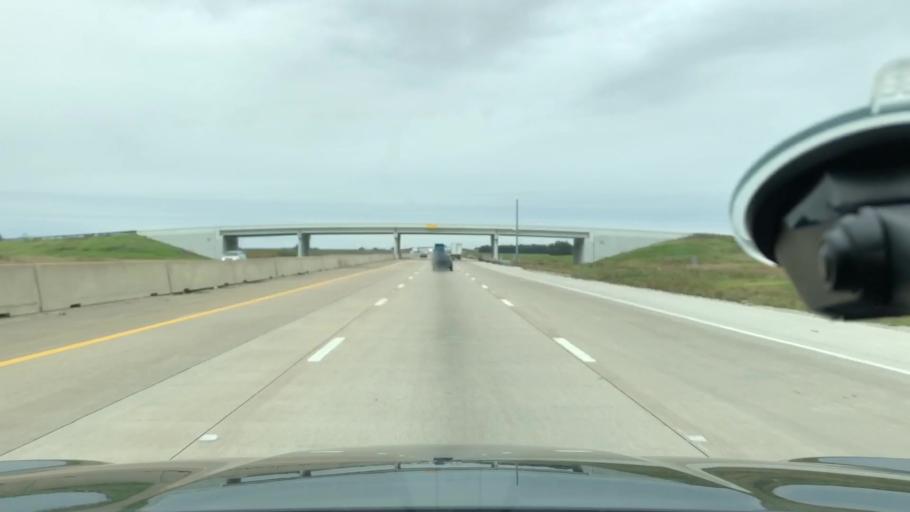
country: US
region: Texas
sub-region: Ellis County
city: Italy
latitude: 32.2448
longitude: -96.8758
